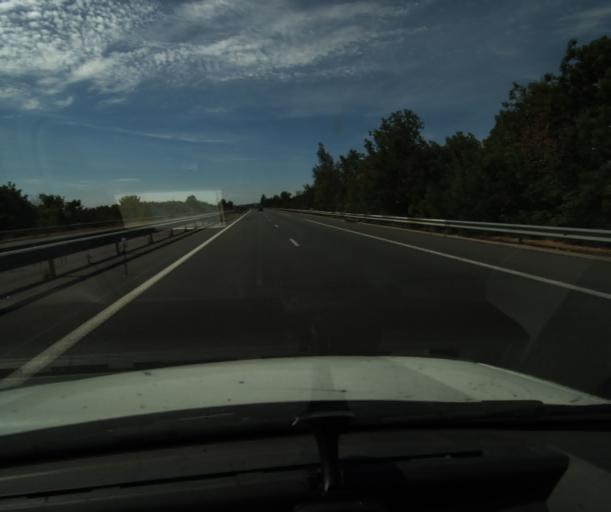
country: FR
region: Midi-Pyrenees
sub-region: Departement du Tarn-et-Garonne
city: Saint-Porquier
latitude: 44.0417
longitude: 1.1496
